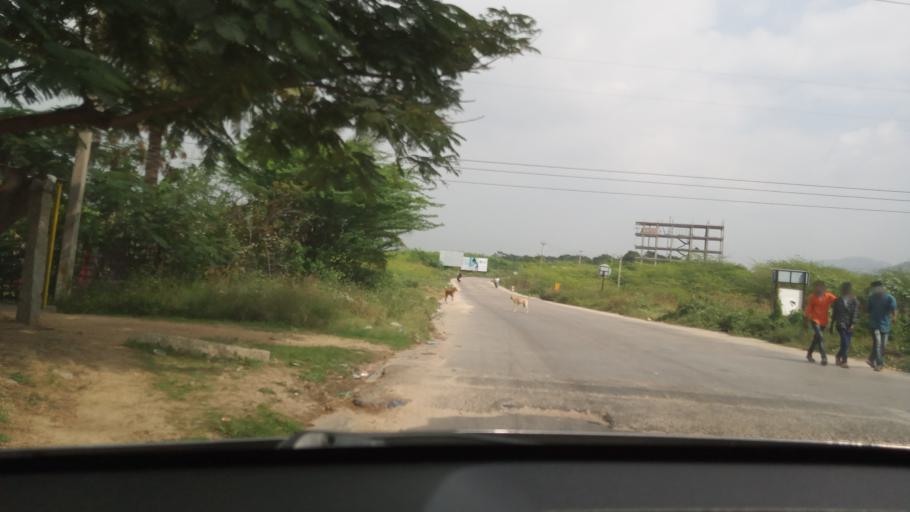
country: IN
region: Andhra Pradesh
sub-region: Chittoor
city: Madanapalle
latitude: 13.6520
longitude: 78.8096
